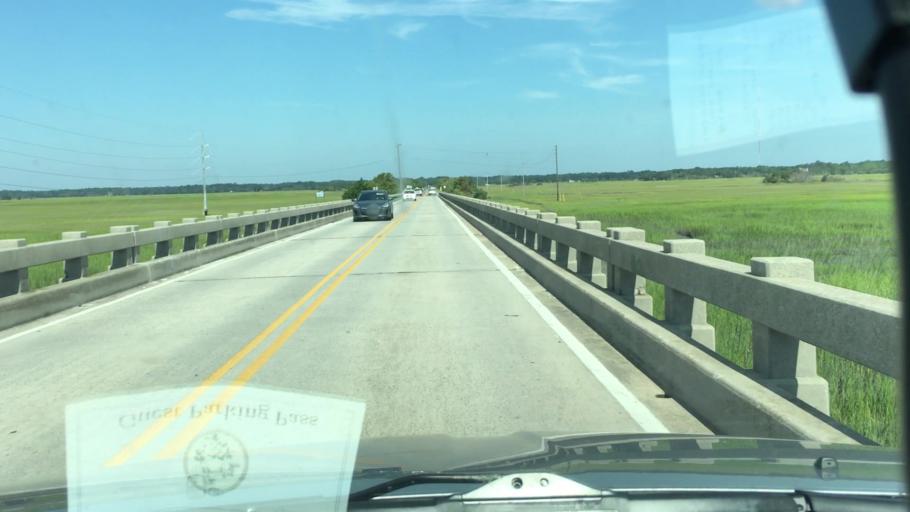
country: US
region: South Carolina
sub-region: Beaufort County
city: Beaufort
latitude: 32.4055
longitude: -80.4566
